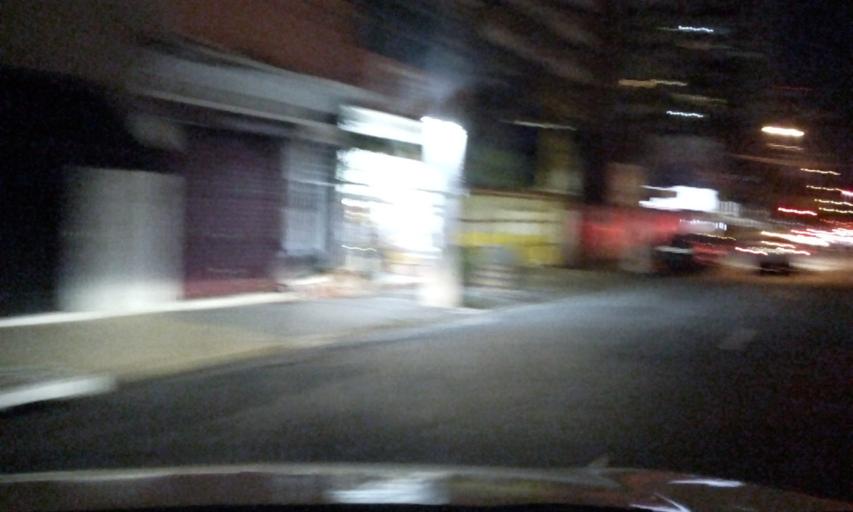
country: BR
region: Sao Paulo
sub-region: Sao Paulo
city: Sao Paulo
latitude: -23.6077
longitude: -46.6615
